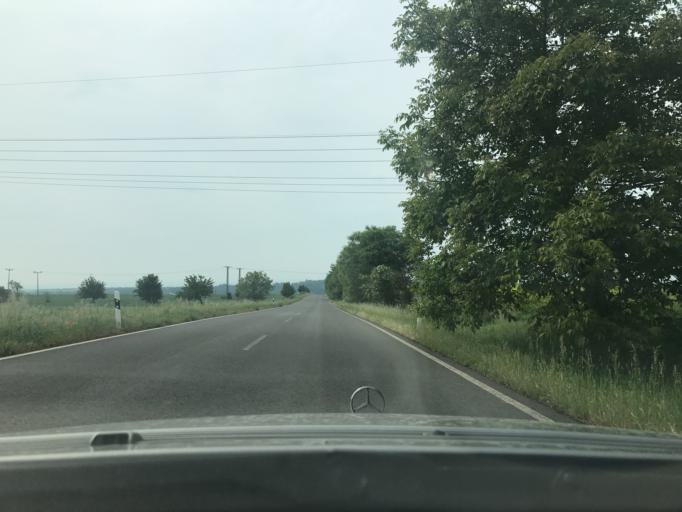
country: DE
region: Thuringia
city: Muehlhausen
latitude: 51.2230
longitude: 10.4920
